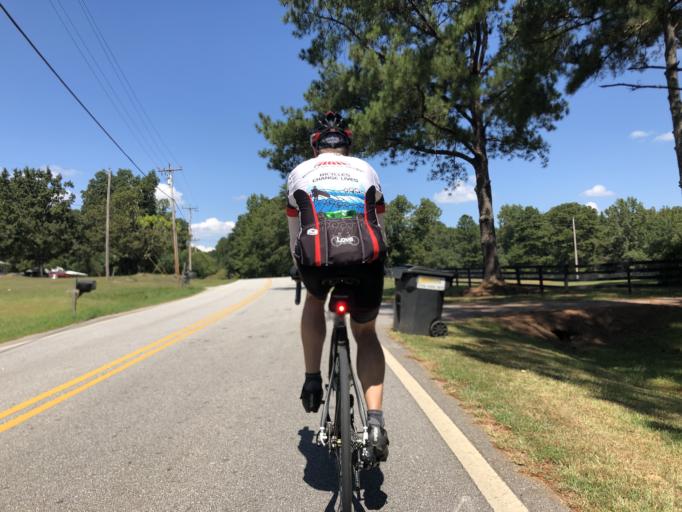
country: US
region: Georgia
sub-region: Fulton County
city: Chattahoochee Hills
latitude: 33.4854
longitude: -84.8002
